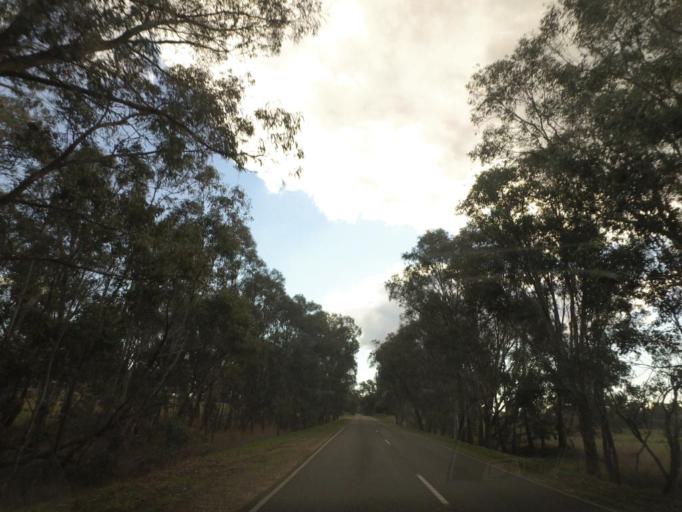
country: AU
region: New South Wales
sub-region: Corowa Shire
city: Howlong
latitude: -36.1891
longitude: 146.6125
